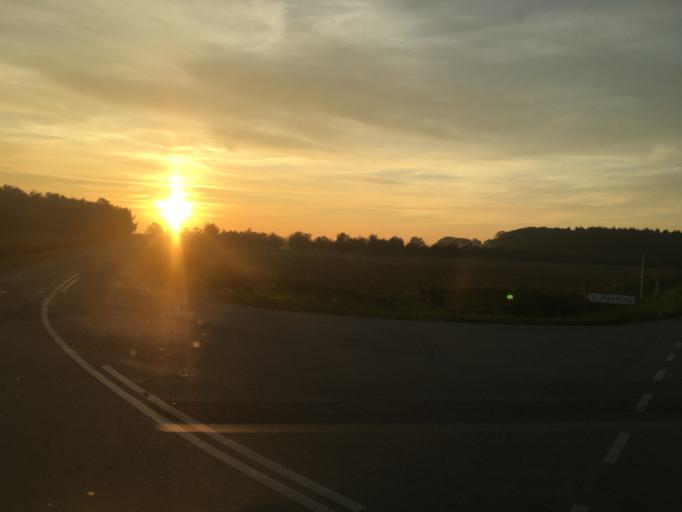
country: DK
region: South Denmark
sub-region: Tonder Kommune
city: Logumkloster
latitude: 55.0182
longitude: 9.1029
